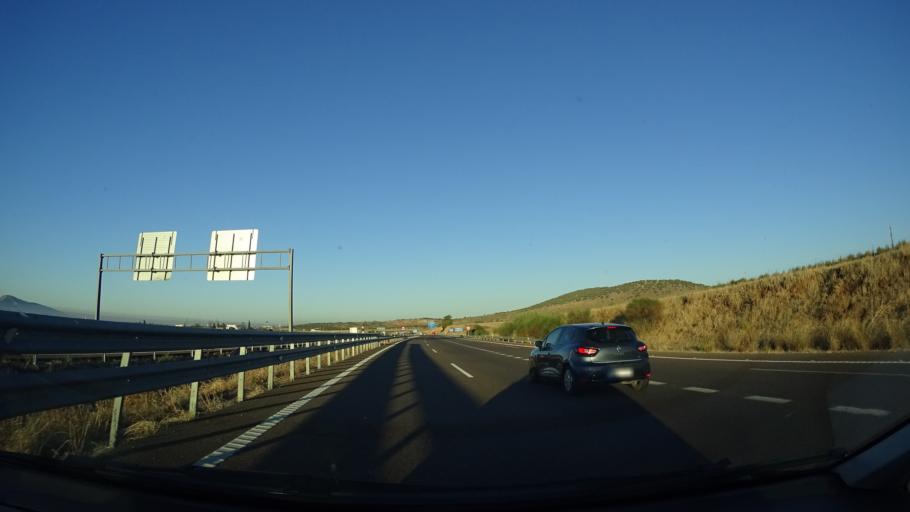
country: ES
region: Extremadura
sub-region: Provincia de Badajoz
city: Merida
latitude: 38.9430
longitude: -6.3481
